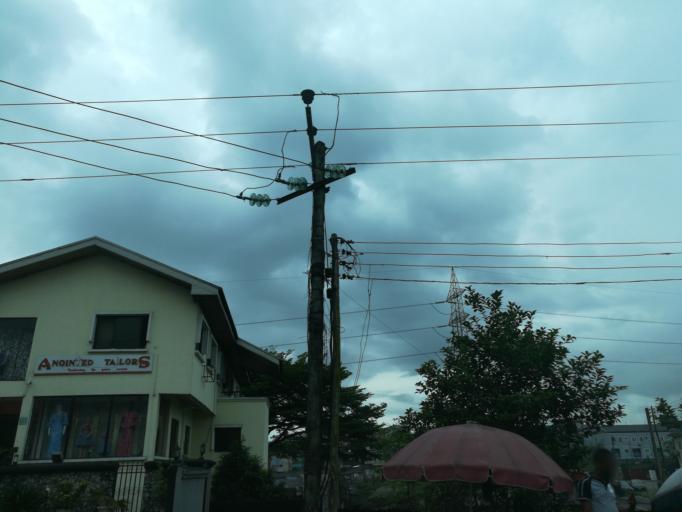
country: NG
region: Rivers
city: Port Harcourt
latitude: 4.8401
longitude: 7.0343
